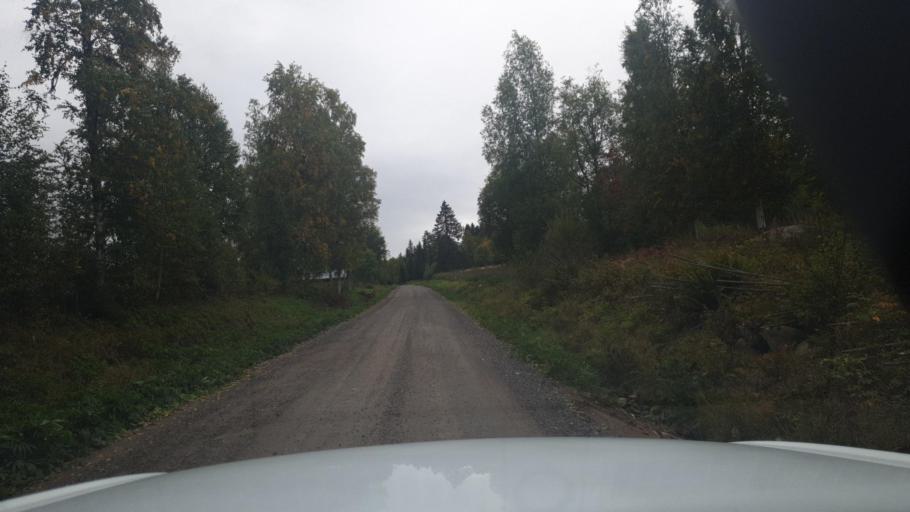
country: SE
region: Vaermland
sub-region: Torsby Kommun
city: Torsby
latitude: 60.1839
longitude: 12.6445
